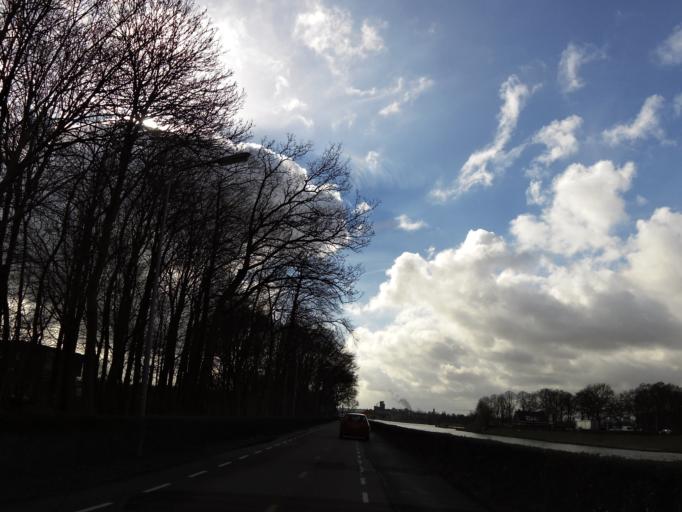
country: NL
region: Limburg
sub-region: Gemeente Maastricht
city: Maastricht
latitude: 50.8714
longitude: 5.7009
